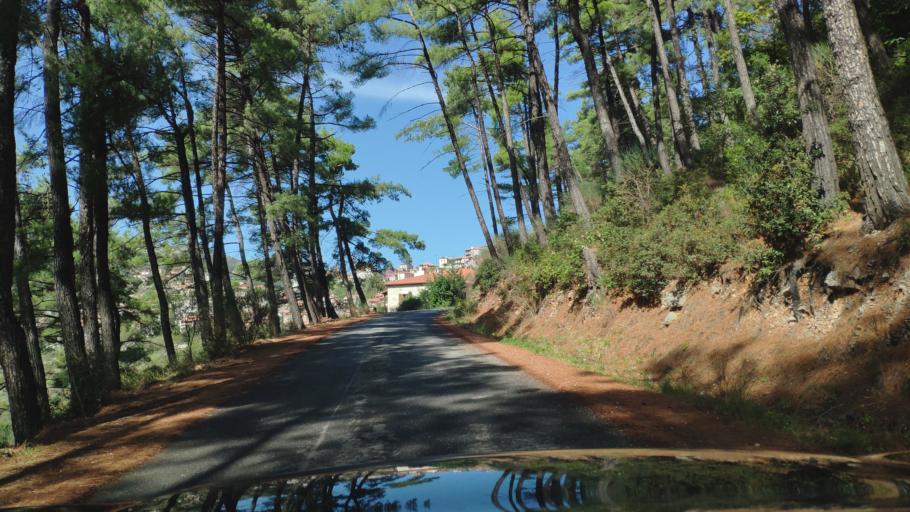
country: GR
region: Peloponnese
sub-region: Nomos Arkadias
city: Dimitsana
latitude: 37.5903
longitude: 22.0427
